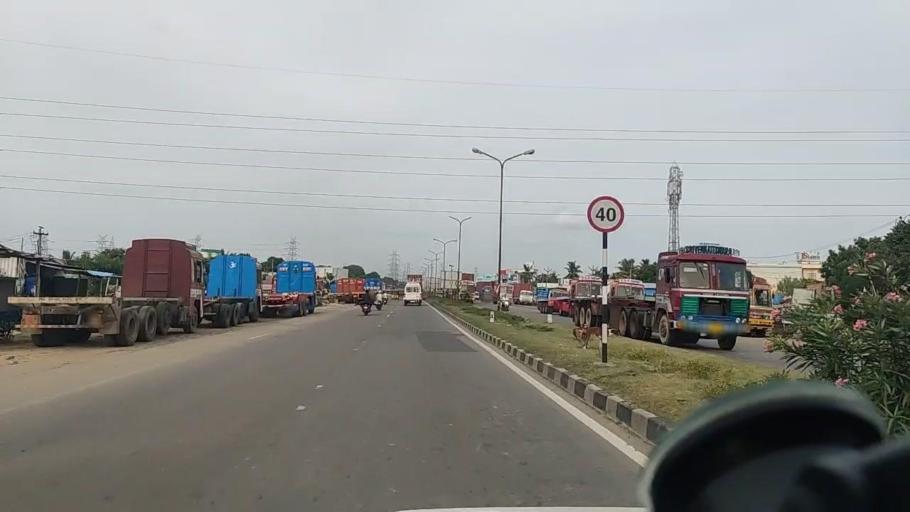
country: IN
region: Tamil Nadu
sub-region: Thiruvallur
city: Chinnasekkadu
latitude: 13.1771
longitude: 80.2462
